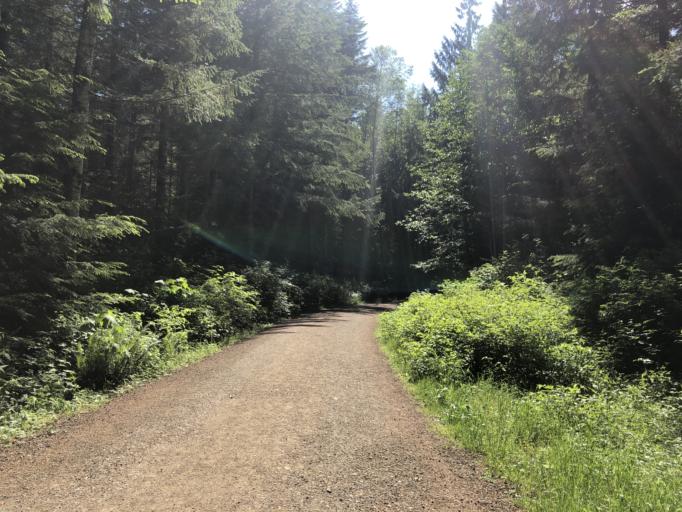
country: US
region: Washington
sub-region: Kitsap County
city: Erlands Point-Kitsap Lake
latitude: 47.5727
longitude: -122.7265
